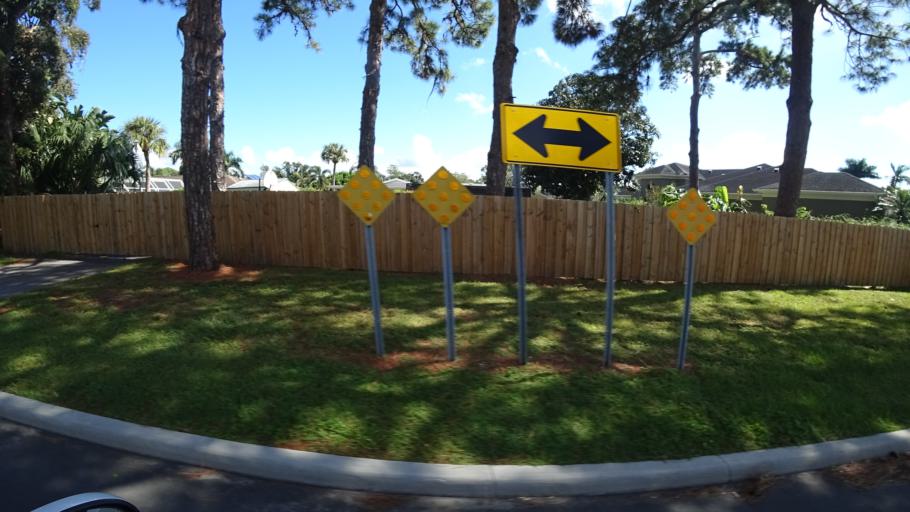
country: US
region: Florida
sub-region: Manatee County
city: West Bradenton
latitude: 27.4907
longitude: -82.6121
